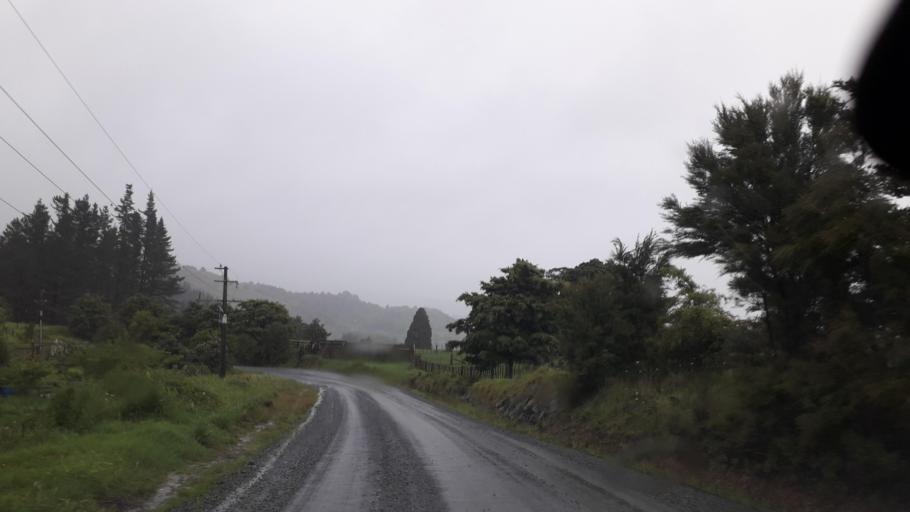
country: NZ
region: Northland
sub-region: Far North District
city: Kerikeri
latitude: -35.1261
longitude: 173.7448
